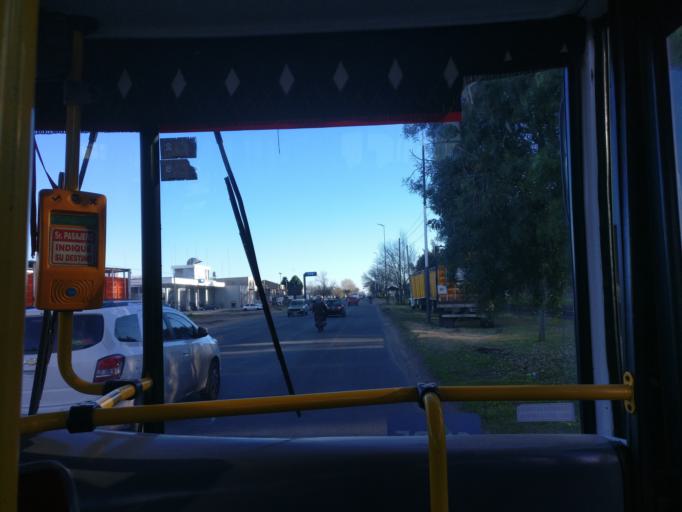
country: AR
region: Buenos Aires
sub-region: Partido de Ezeiza
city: Ezeiza
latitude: -34.8986
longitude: -58.5795
